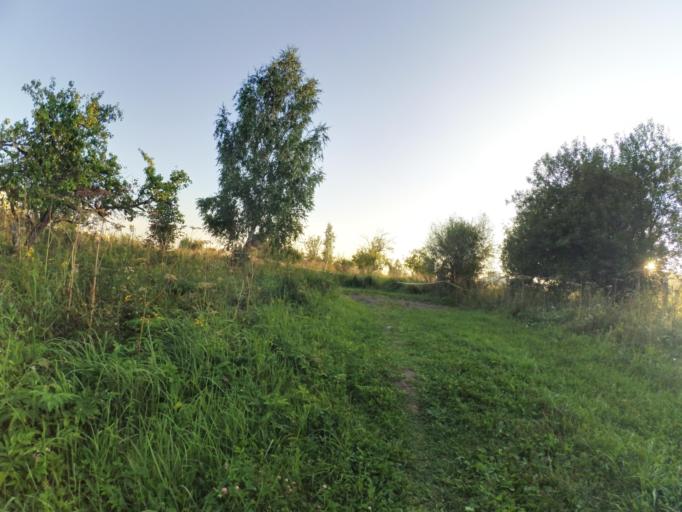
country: RU
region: Moscow
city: Strogino
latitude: 55.8605
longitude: 37.4021
